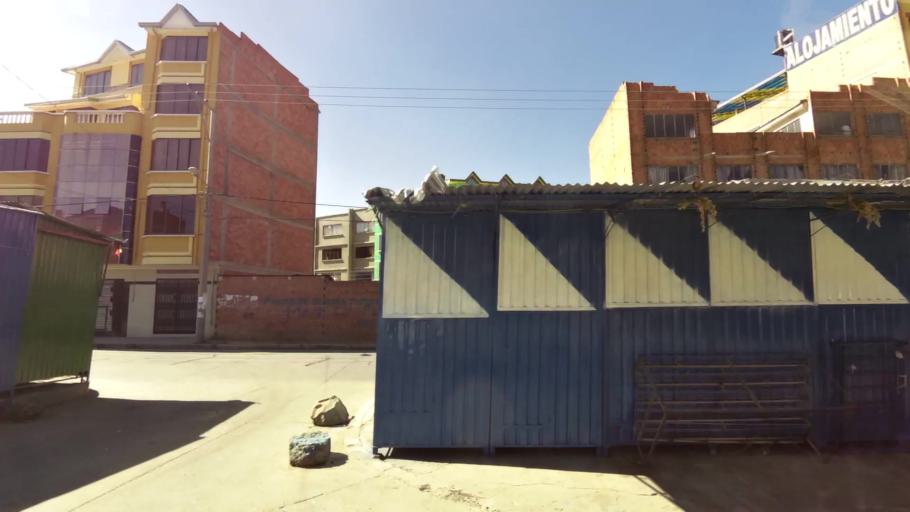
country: BO
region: La Paz
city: La Paz
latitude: -16.5150
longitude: -68.1616
